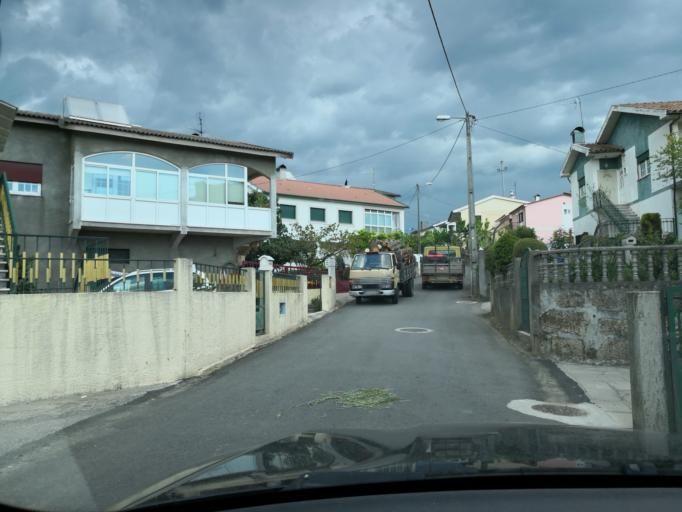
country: PT
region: Vila Real
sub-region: Vila Real
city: Vila Real
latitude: 41.2662
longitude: -7.6905
